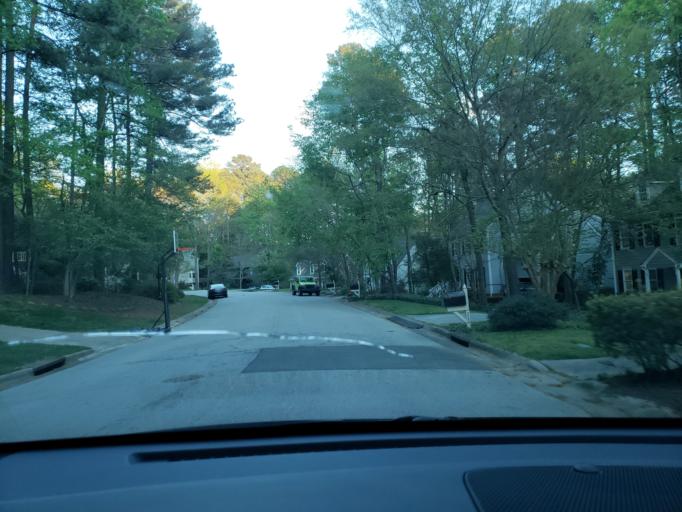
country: US
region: North Carolina
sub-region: Durham County
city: Durham
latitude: 35.9201
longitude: -78.9475
